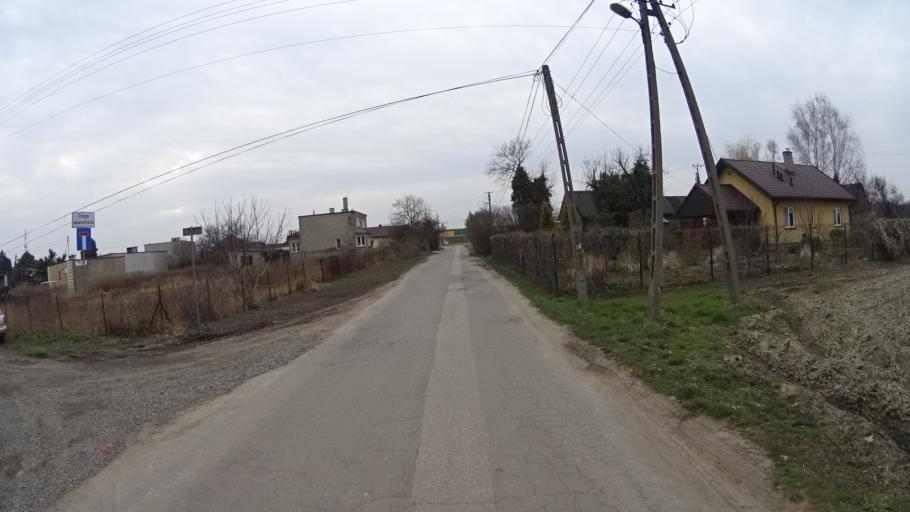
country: PL
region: Masovian Voivodeship
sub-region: Warszawa
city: Ursus
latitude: 52.2092
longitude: 20.8615
